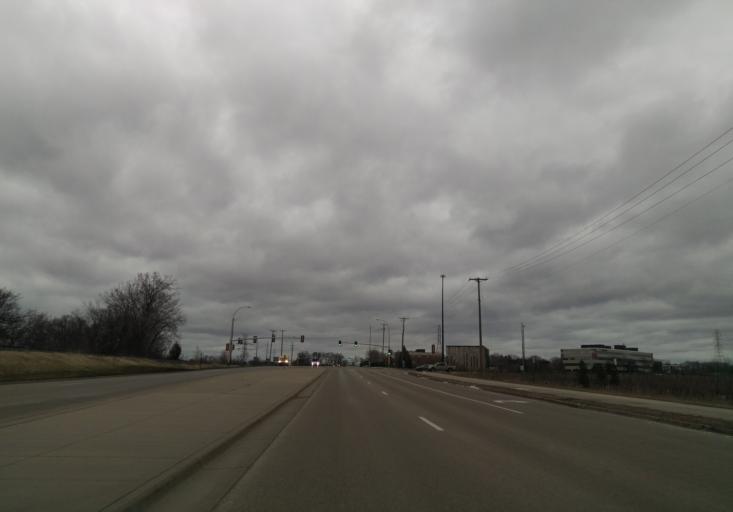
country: US
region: Minnesota
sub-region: Hennepin County
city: Edina
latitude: 44.8570
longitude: -93.3627
